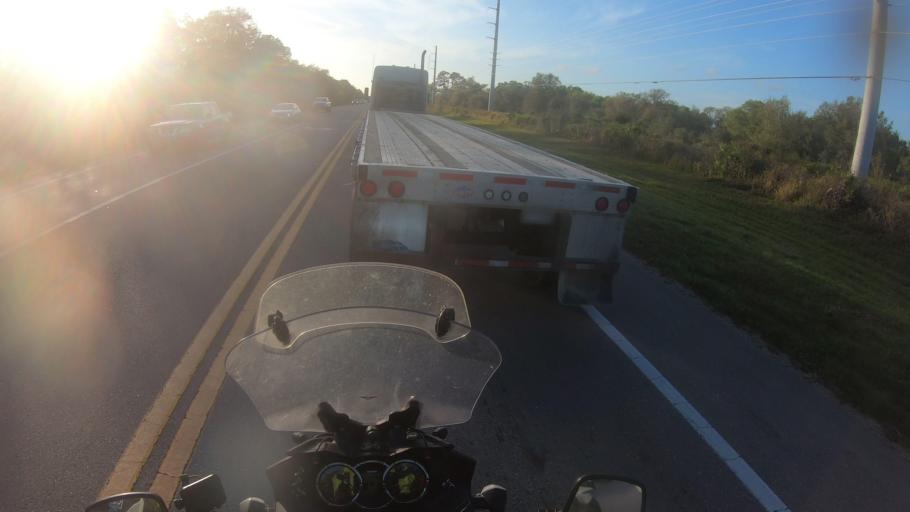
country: US
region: Florida
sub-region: Sarasota County
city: The Meadows
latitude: 27.4167
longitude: -82.3554
